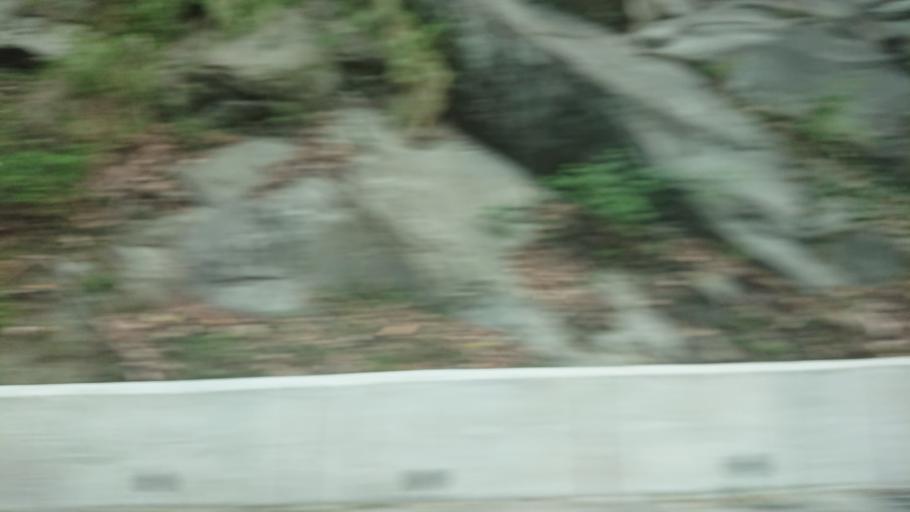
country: TW
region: Taiwan
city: Daxi
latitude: 24.8751
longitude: 121.3839
